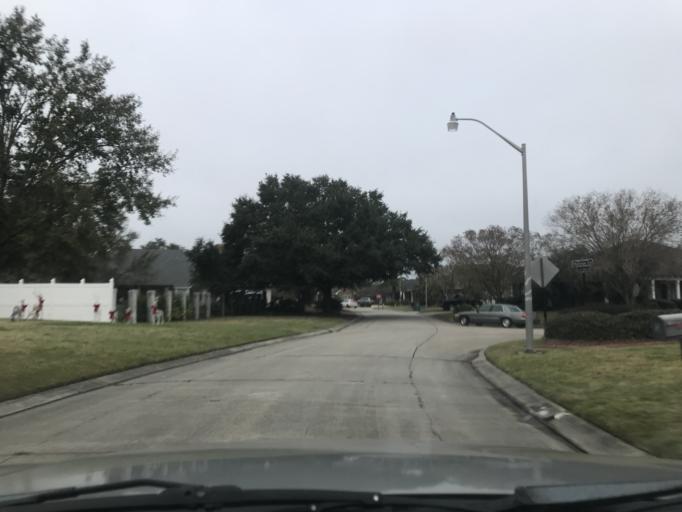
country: US
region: Louisiana
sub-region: Jefferson Parish
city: Woodmere
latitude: 29.8684
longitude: -90.0942
